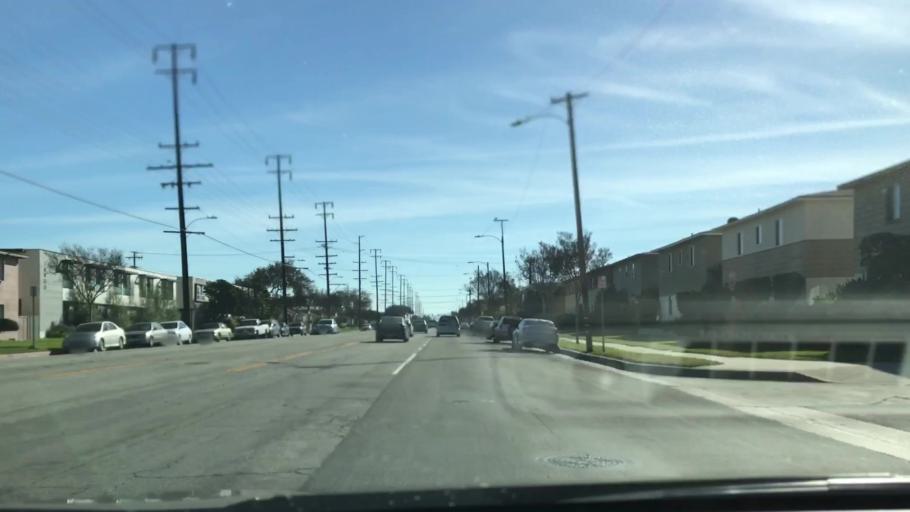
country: US
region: California
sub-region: Los Angeles County
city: Alondra Park
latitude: 33.8779
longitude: -118.3266
